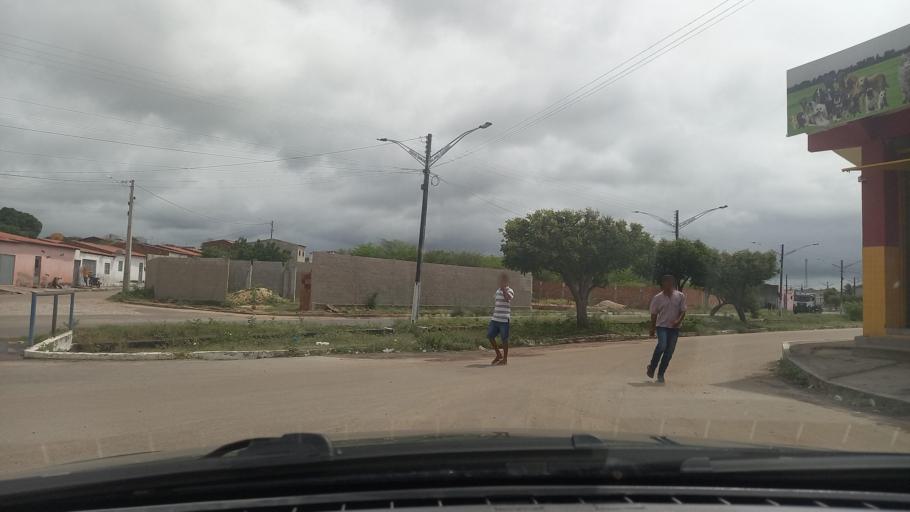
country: BR
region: Alagoas
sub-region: Delmiro Gouveia
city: Delmiro Gouveia
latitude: -9.3898
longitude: -38.0006
